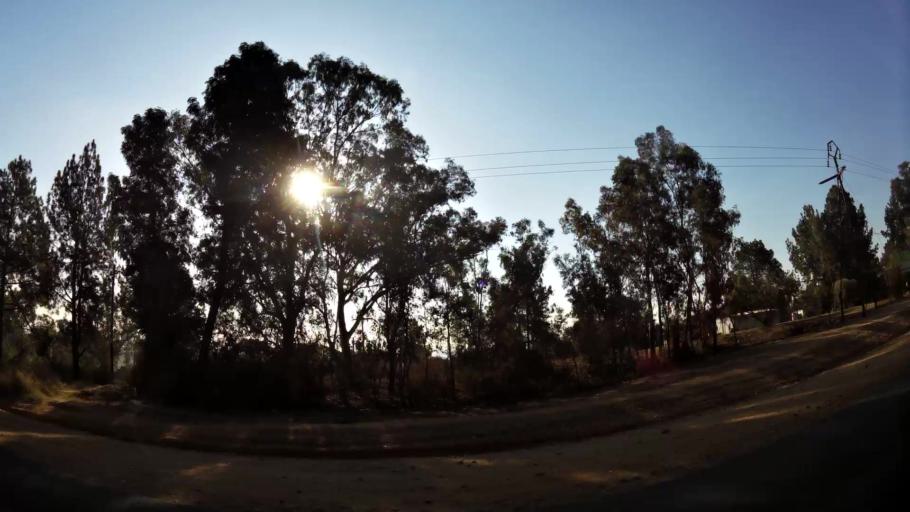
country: ZA
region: Gauteng
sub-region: West Rand District Municipality
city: Muldersdriseloop
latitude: -26.0192
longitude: 27.8814
